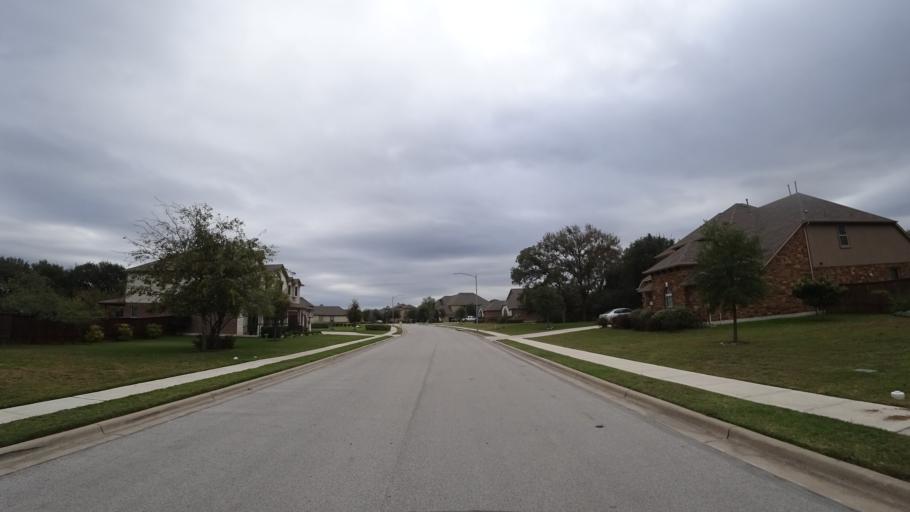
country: US
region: Texas
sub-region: Travis County
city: Manchaca
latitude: 30.1437
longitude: -97.8542
